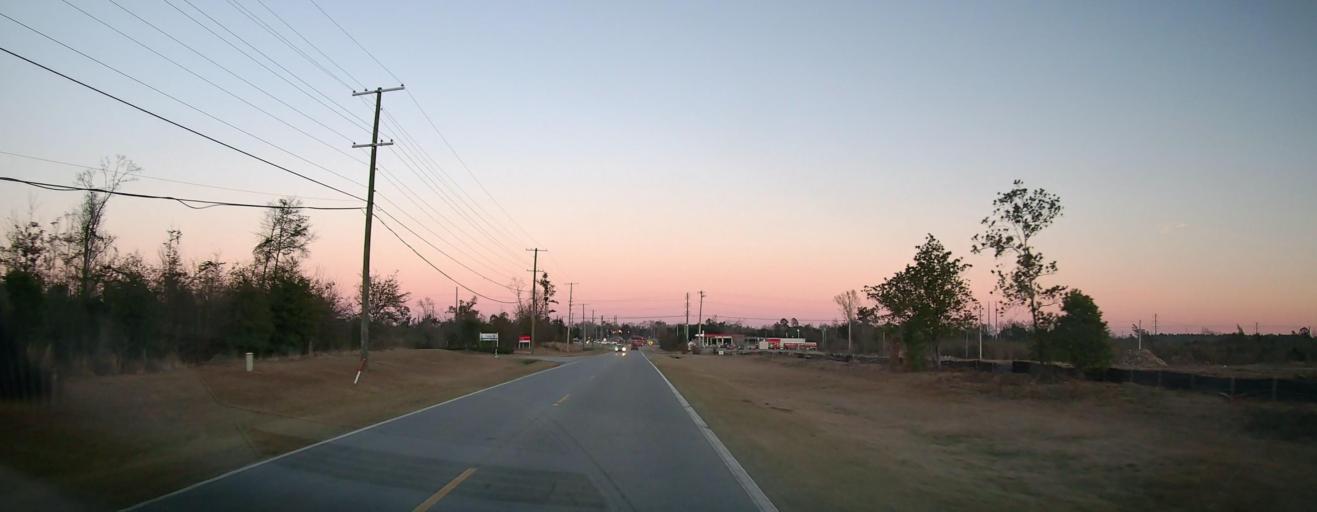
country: US
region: Georgia
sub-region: Dougherty County
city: Putney
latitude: 31.5292
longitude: -84.1194
